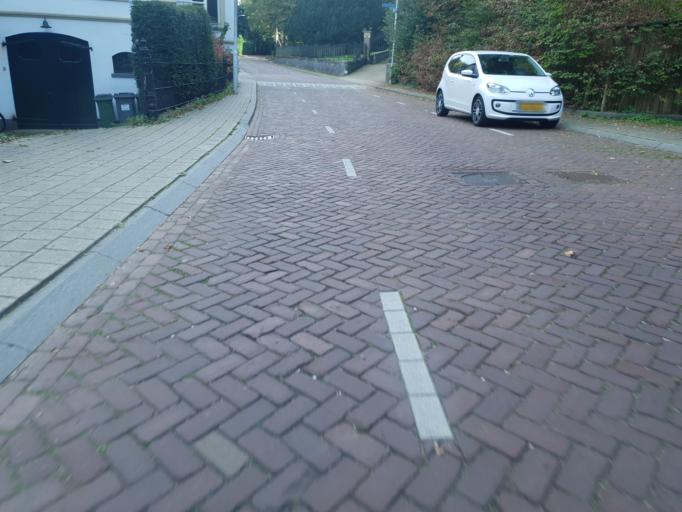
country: NL
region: Gelderland
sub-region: Gemeente Groesbeek
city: Berg en Dal
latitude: 51.8371
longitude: 5.9003
